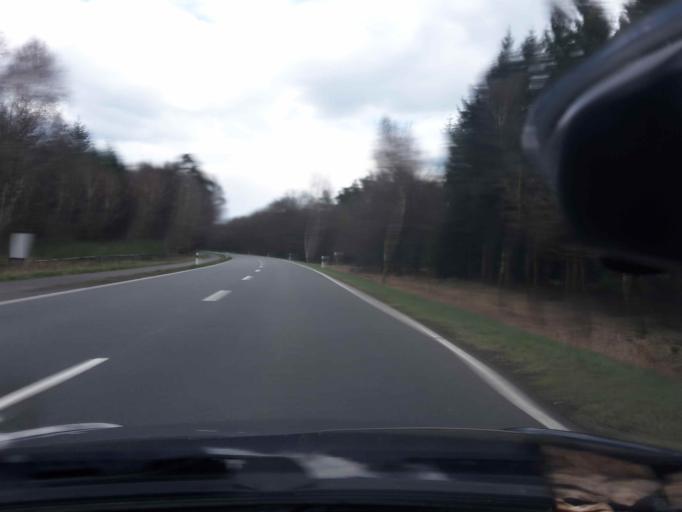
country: DE
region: Lower Saxony
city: Bispingen
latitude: 53.0830
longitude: 9.9341
